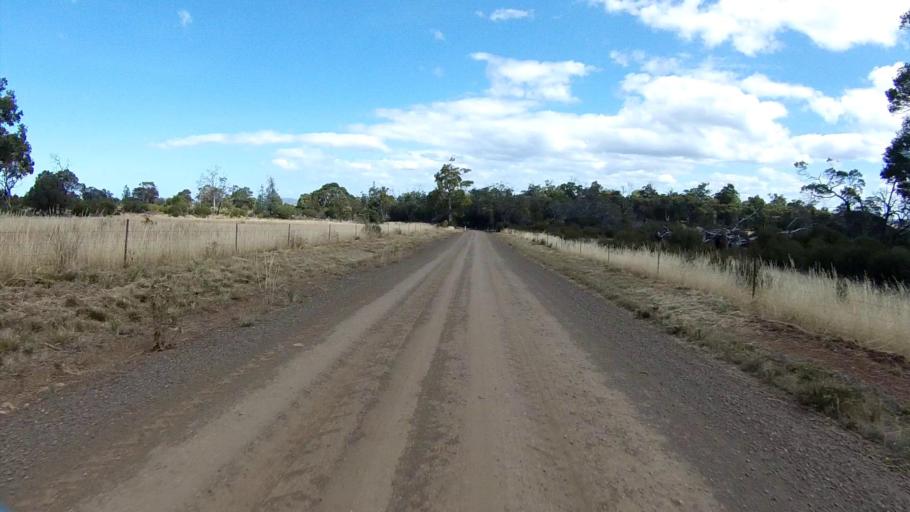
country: AU
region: Tasmania
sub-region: Break O'Day
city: St Helens
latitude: -41.9817
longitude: 148.0661
